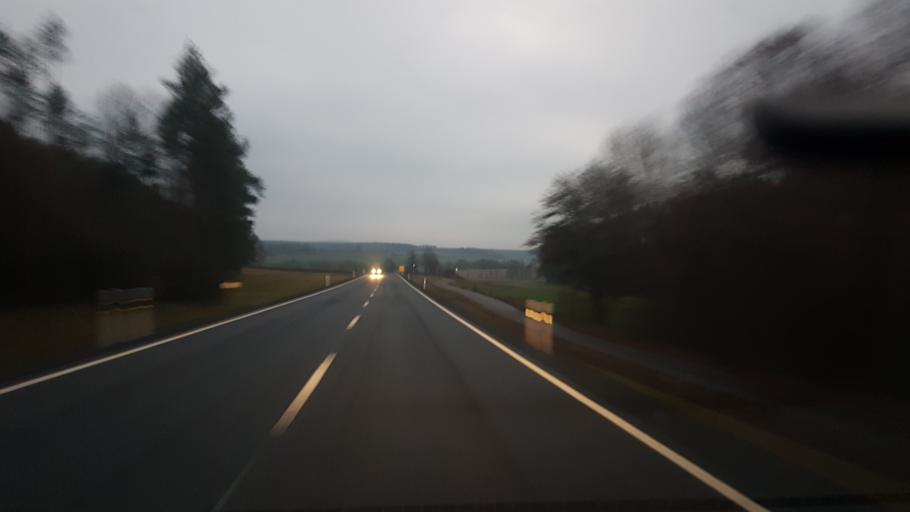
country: DE
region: Bavaria
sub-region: Regierungsbezirk Unterfranken
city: Ermershausen
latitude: 50.2278
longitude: 10.5801
